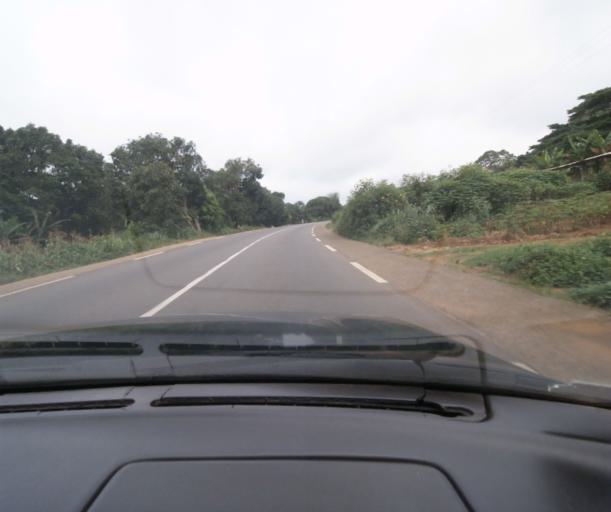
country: CM
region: Centre
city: Obala
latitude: 4.1879
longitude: 11.4575
